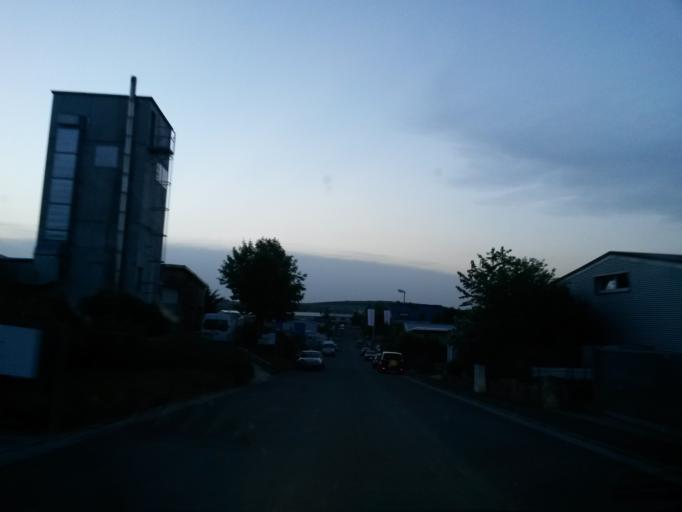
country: DE
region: Bavaria
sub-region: Regierungsbezirk Unterfranken
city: Rimpar
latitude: 49.8449
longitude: 9.9677
